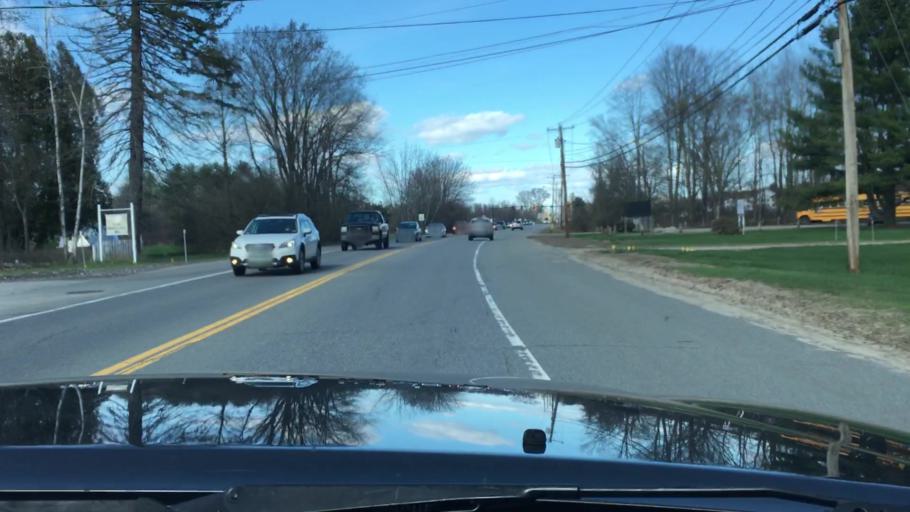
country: US
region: New Hampshire
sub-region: Merrimack County
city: Concord
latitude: 43.1862
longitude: -71.5582
